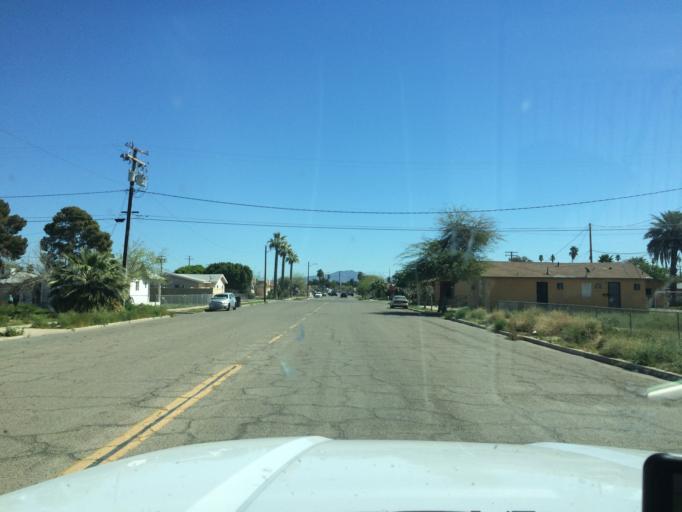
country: US
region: California
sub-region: Riverside County
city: Blythe
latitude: 33.6123
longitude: -114.5940
